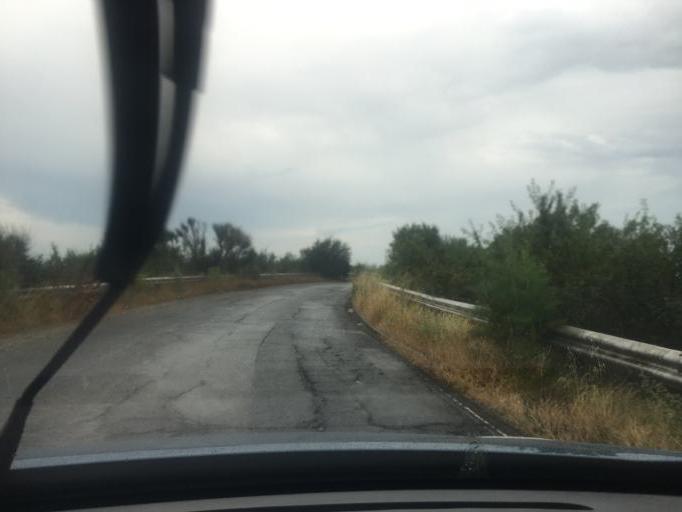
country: BG
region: Burgas
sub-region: Obshtina Burgas
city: Burgas
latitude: 42.5535
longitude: 27.4914
